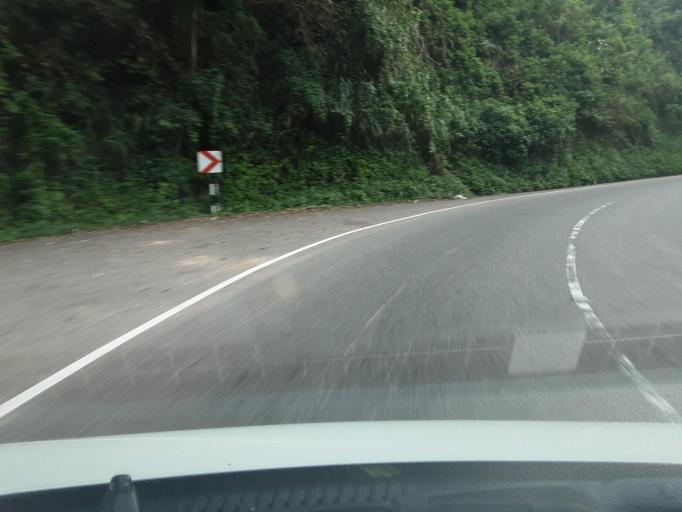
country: LK
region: Uva
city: Badulla
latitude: 6.9474
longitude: 81.0185
